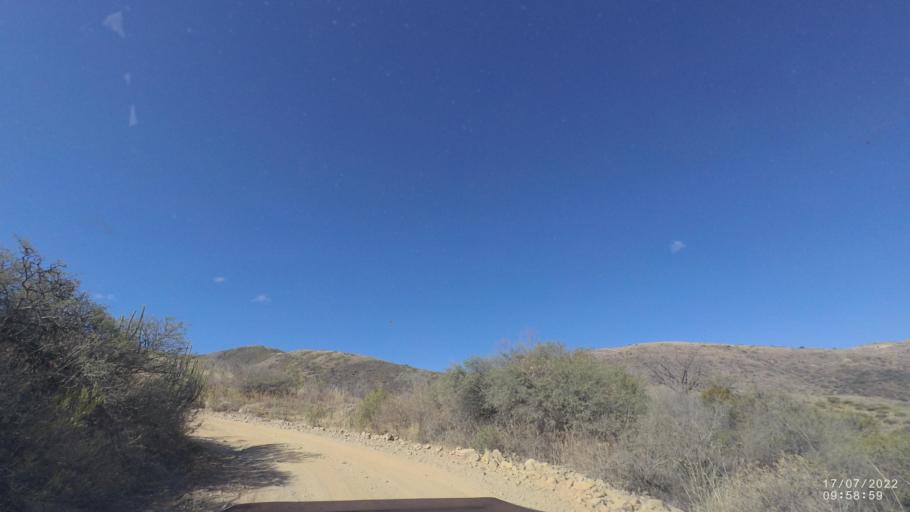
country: BO
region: Cochabamba
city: Capinota
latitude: -17.6011
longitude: -66.1895
